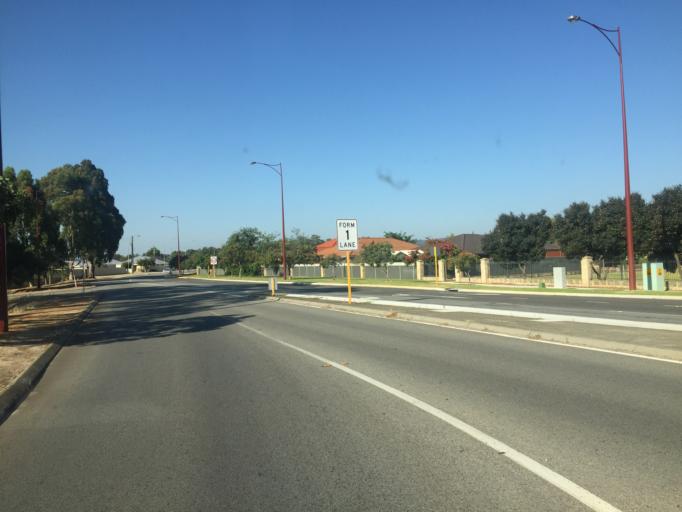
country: AU
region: Western Australia
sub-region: Canning
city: East Cannington
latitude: -32.0046
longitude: 115.9802
